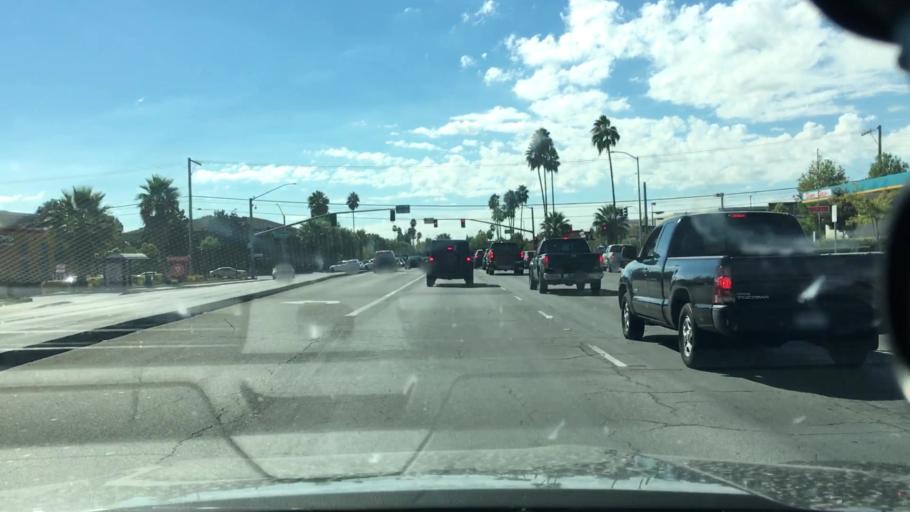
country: US
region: California
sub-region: Sacramento County
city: Arden-Arcade
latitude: 38.6115
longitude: -121.3830
